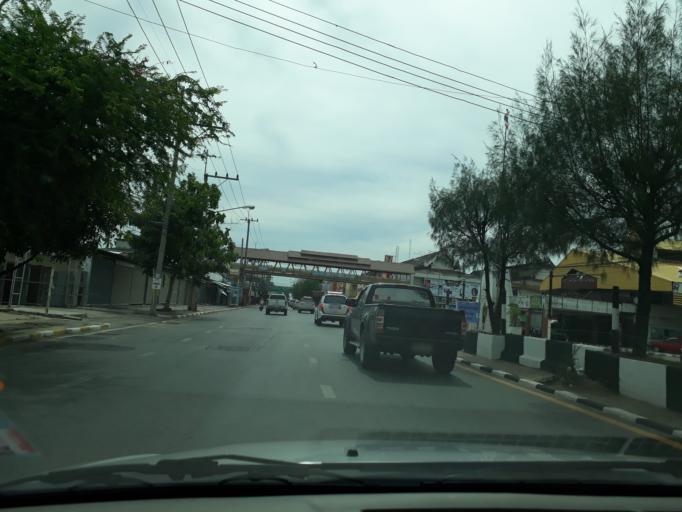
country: TH
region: Khon Kaen
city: Khon Kaen
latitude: 16.4389
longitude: 102.8340
